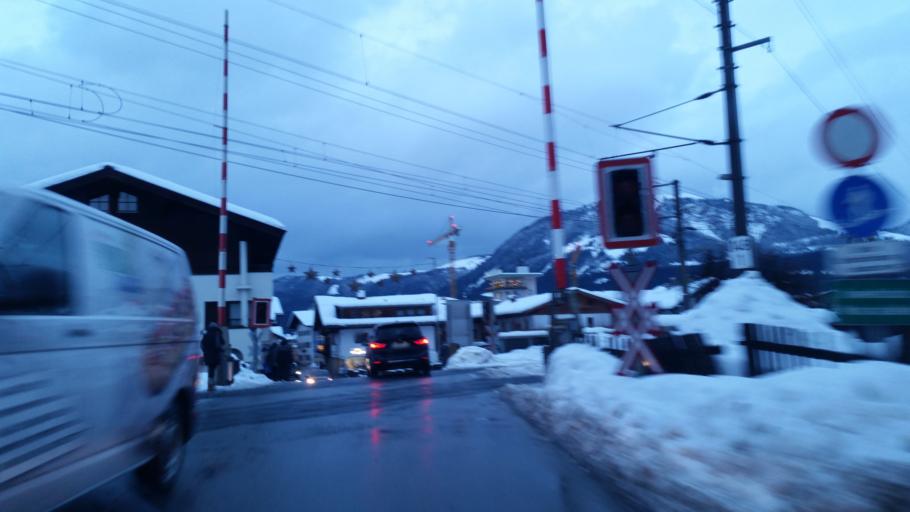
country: AT
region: Tyrol
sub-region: Politischer Bezirk Kitzbuhel
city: Sankt Johann in Tirol
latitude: 47.5196
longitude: 12.4246
